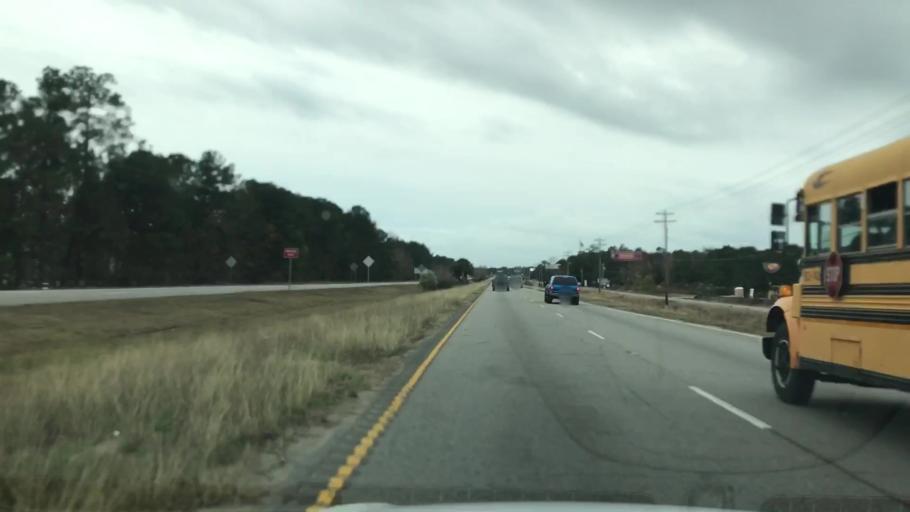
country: US
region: South Carolina
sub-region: Horry County
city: Garden City
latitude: 33.6067
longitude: -79.0153
